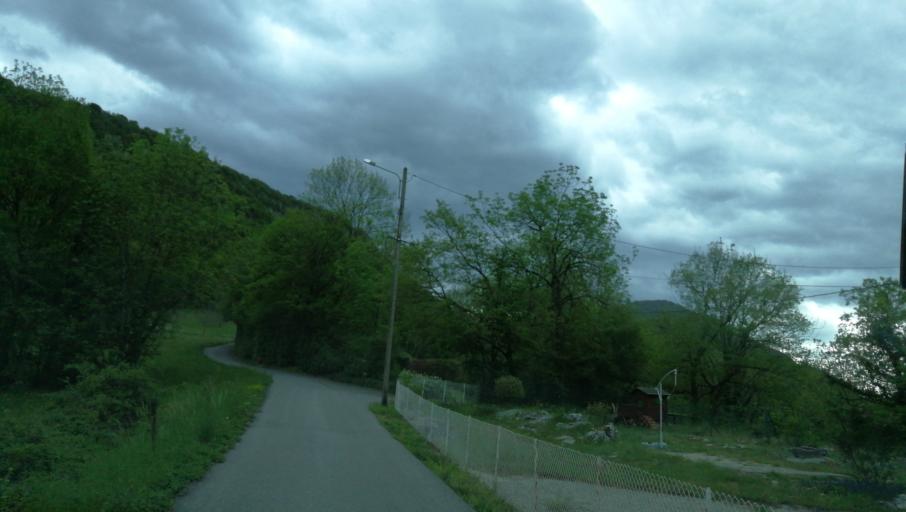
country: FR
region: Rhone-Alpes
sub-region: Departement de la Savoie
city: Chatillon
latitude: 45.7796
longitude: 5.8183
